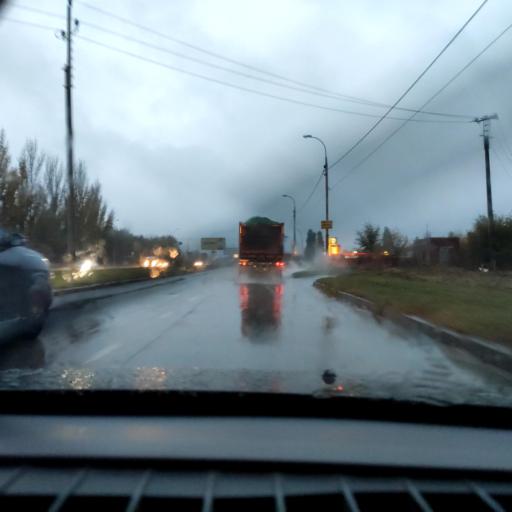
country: RU
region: Samara
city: Tol'yatti
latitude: 53.5609
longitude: 49.2938
